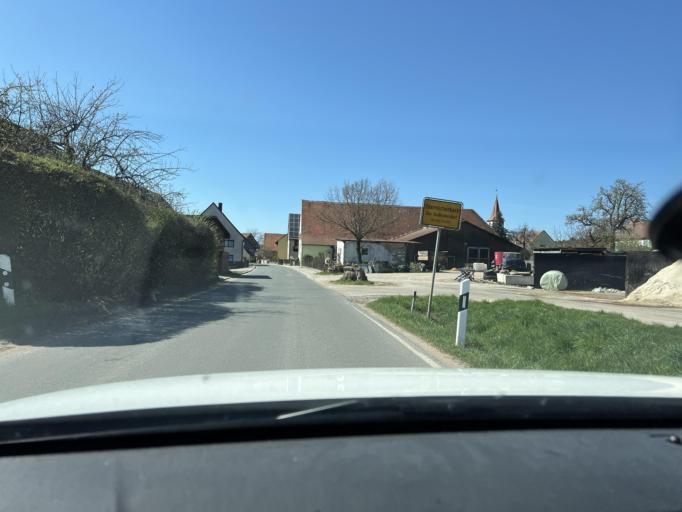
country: DE
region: Bavaria
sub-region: Regierungsbezirk Mittelfranken
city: Grosshabersdorf
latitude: 49.4328
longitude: 10.7606
